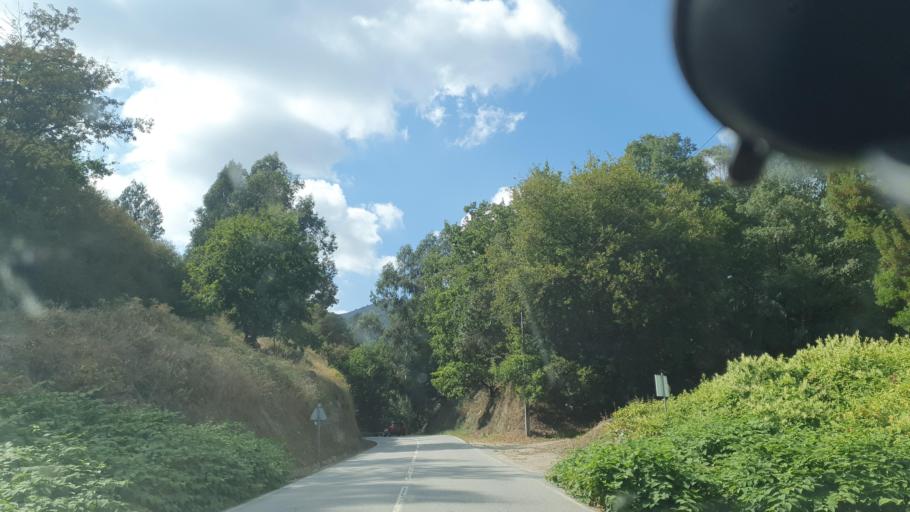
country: PT
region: Braga
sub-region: Vieira do Minho
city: Real
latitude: 41.7044
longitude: -8.2142
